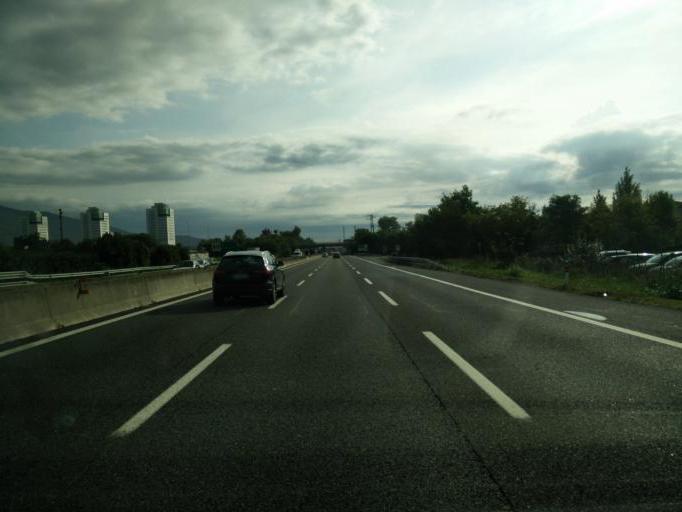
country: IT
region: Lombardy
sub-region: Provincia di Brescia
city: Folzano
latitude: 45.5200
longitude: 10.1864
